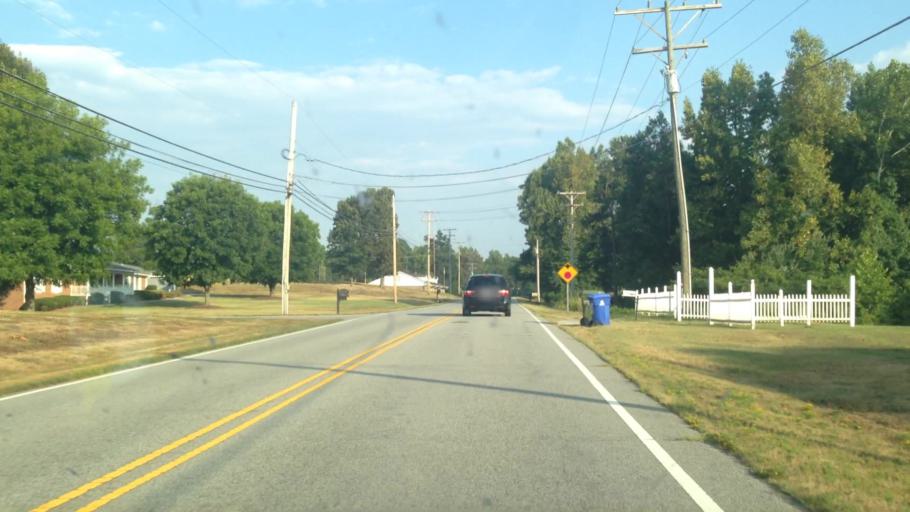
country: US
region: North Carolina
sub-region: Davidson County
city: Thomasville
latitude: 35.9417
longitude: -80.0735
